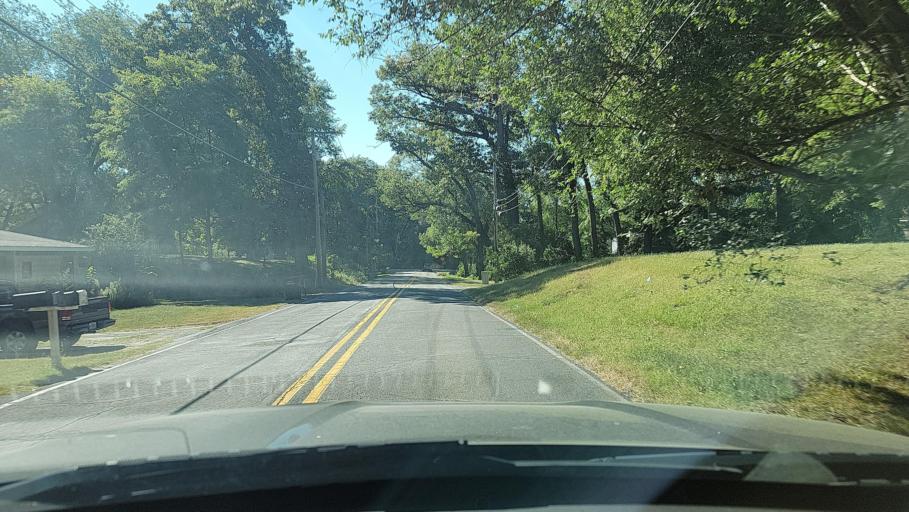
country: US
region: Indiana
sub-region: Porter County
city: Portage
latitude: 41.5940
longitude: -87.1818
